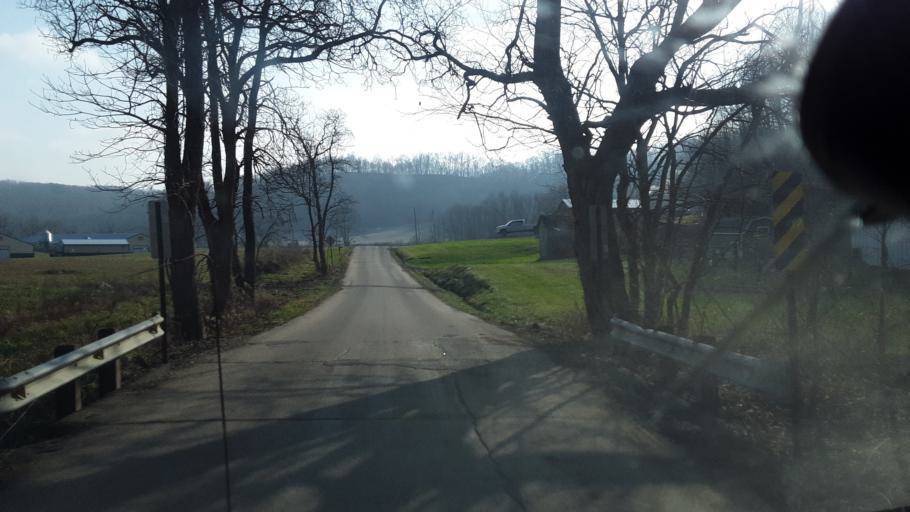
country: US
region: Ohio
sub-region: Knox County
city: Oak Hill
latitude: 40.4324
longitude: -82.2034
